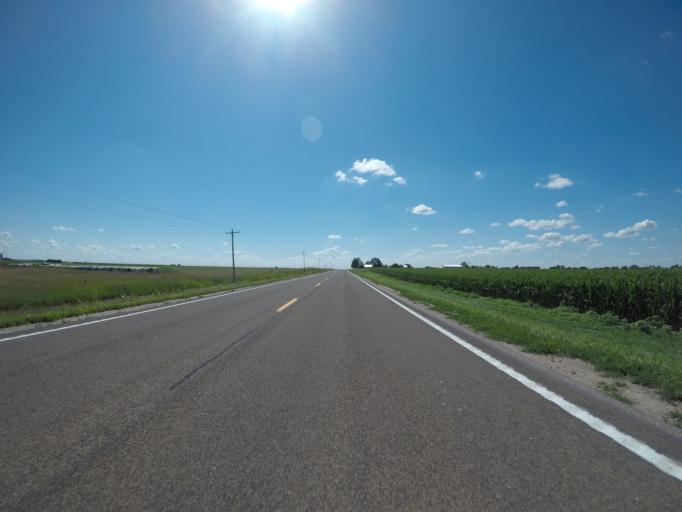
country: US
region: Nebraska
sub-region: Chase County
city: Imperial
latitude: 40.5376
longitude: -101.8502
